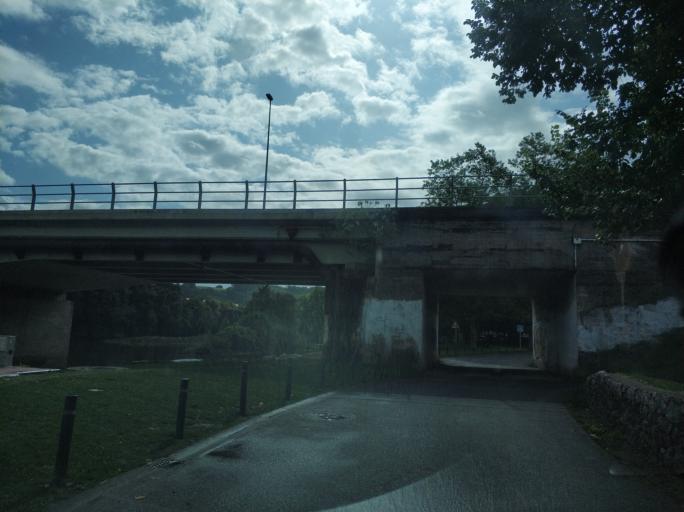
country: ES
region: Cantabria
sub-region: Provincia de Cantabria
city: Miengo
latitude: 43.4037
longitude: -3.9506
